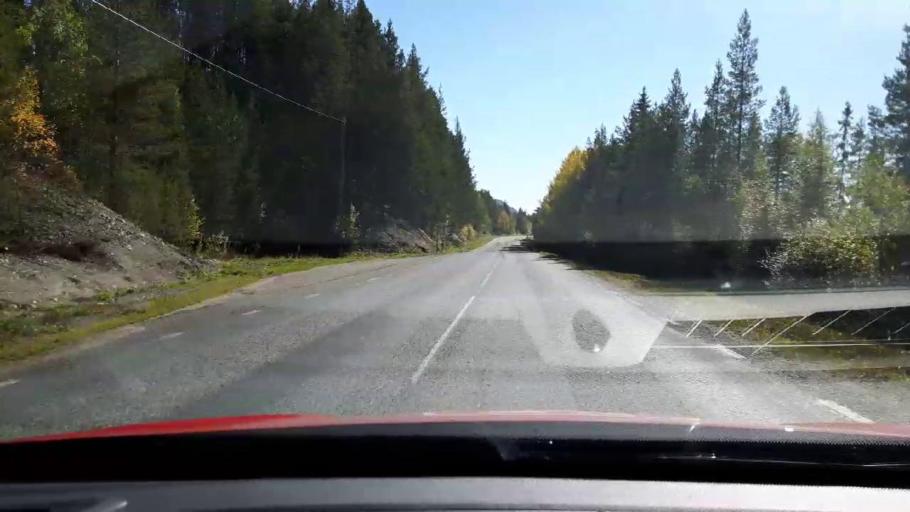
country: SE
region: Jaemtland
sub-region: Harjedalens Kommun
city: Sveg
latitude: 62.4267
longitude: 13.8959
